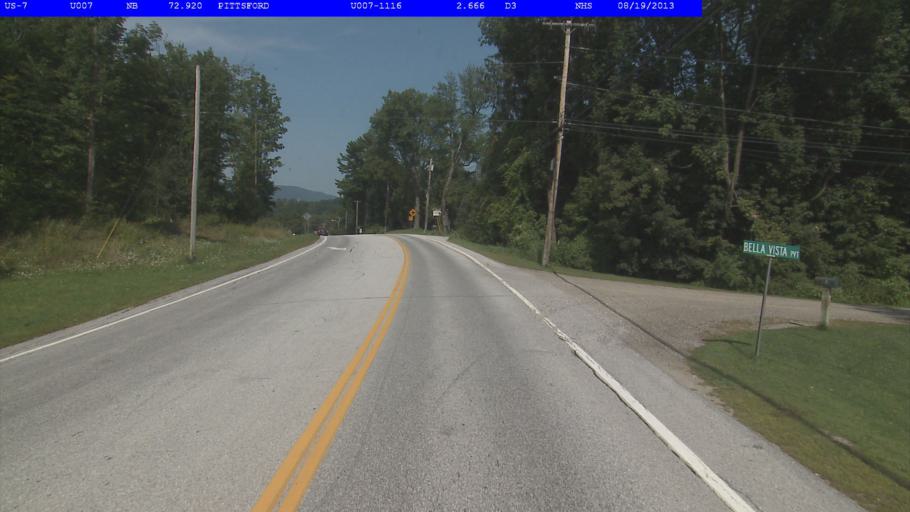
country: US
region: Vermont
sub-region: Rutland County
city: Rutland
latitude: 43.6994
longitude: -73.0073
